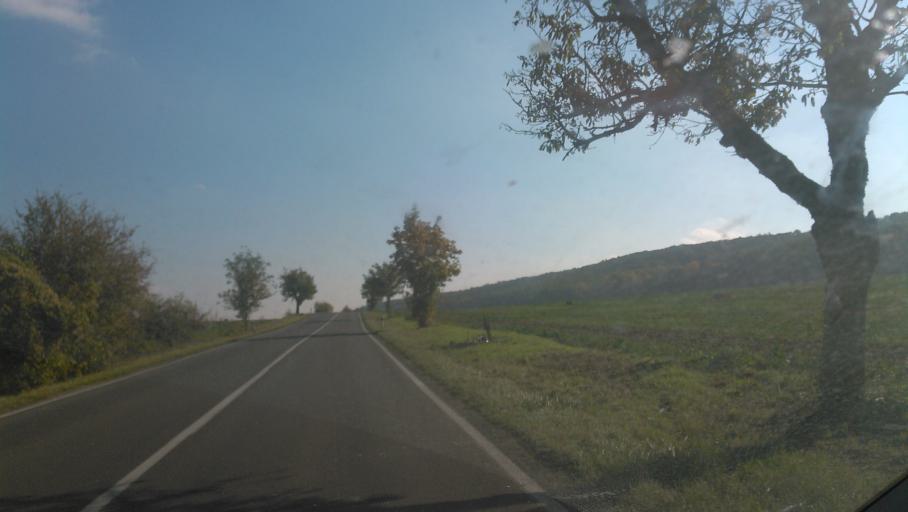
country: SK
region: Trnavsky
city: Hlohovec
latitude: 48.4080
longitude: 17.8407
